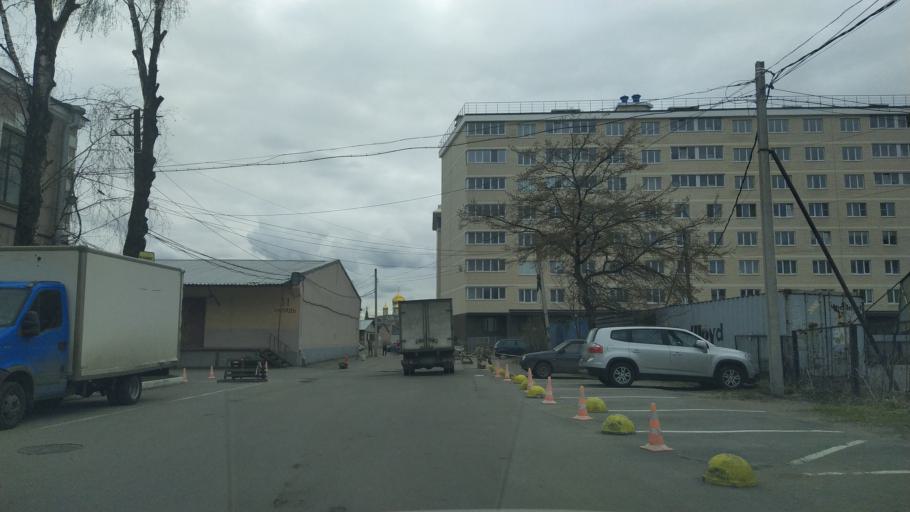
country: RU
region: St.-Petersburg
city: Saint Petersburg
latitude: 59.9027
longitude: 30.3272
